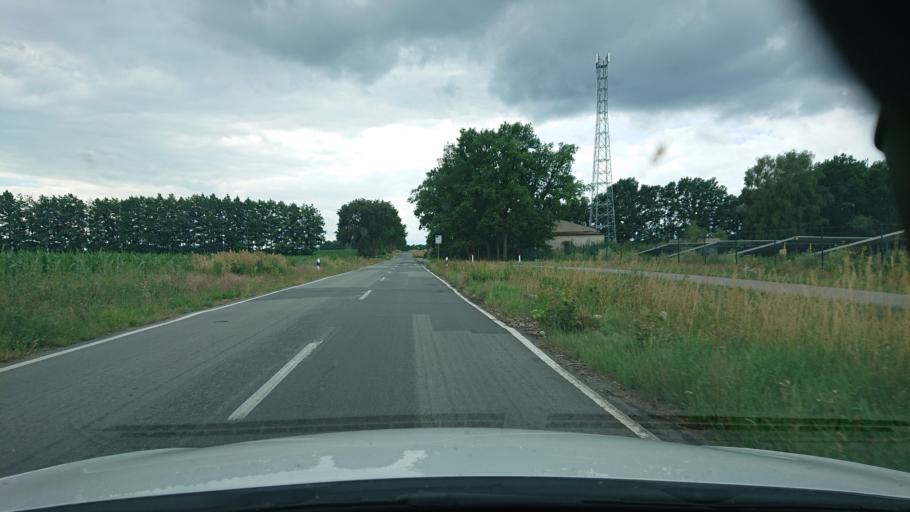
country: DE
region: Mecklenburg-Vorpommern
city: Ludwigslust
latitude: 53.3399
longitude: 11.4025
